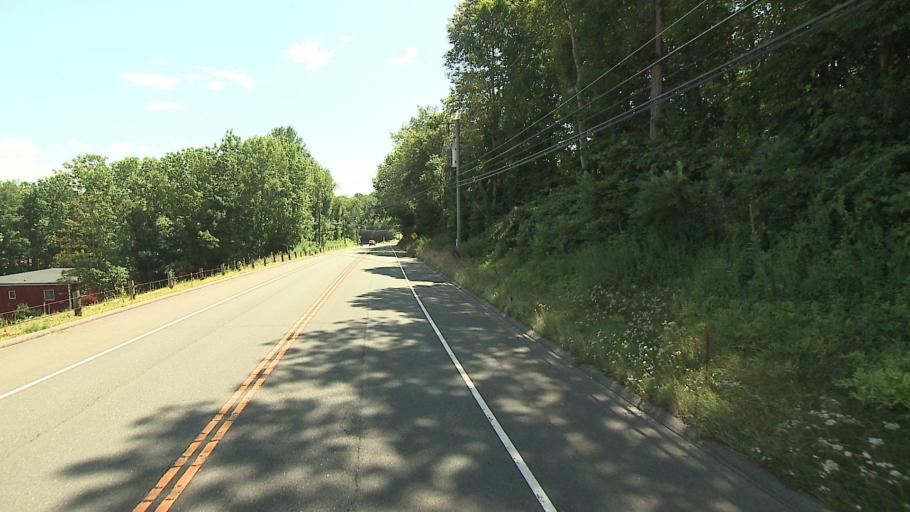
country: US
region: Connecticut
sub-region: Litchfield County
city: Northwest Harwinton
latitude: 41.7853
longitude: -73.0729
